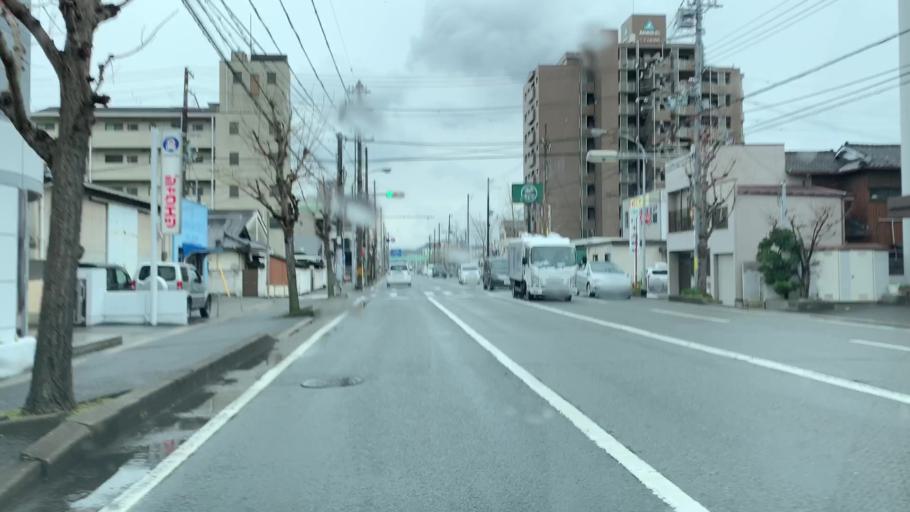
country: JP
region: Wakayama
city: Wakayama-shi
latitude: 34.2218
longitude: 135.1596
